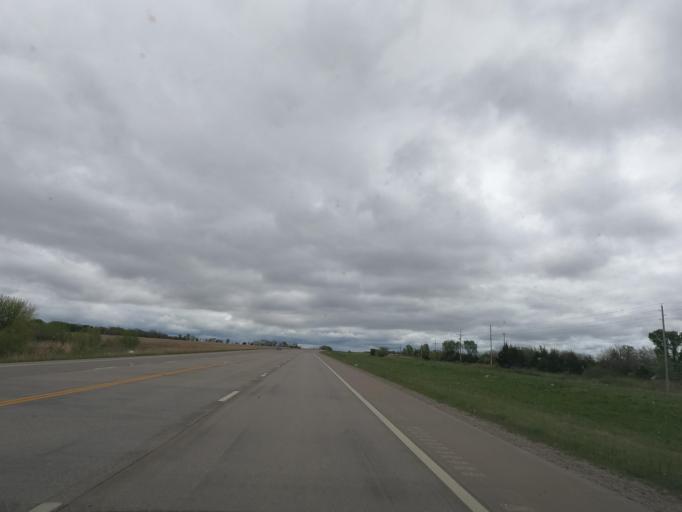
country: US
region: Kansas
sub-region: Elk County
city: Howard
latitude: 37.6355
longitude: -96.1766
